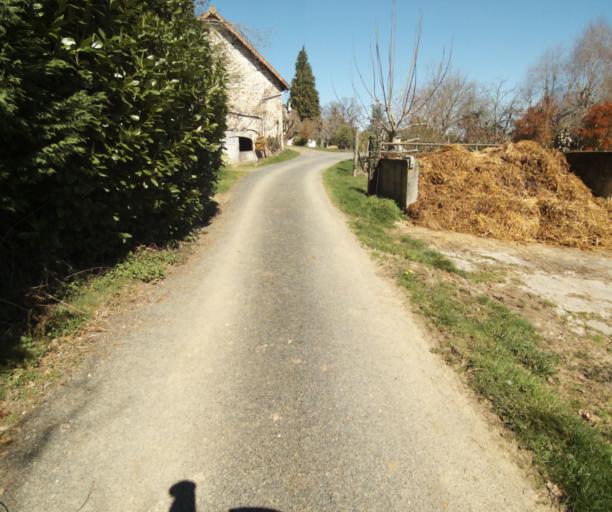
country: FR
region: Limousin
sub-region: Departement de la Correze
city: Saint-Clement
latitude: 45.3196
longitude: 1.6670
